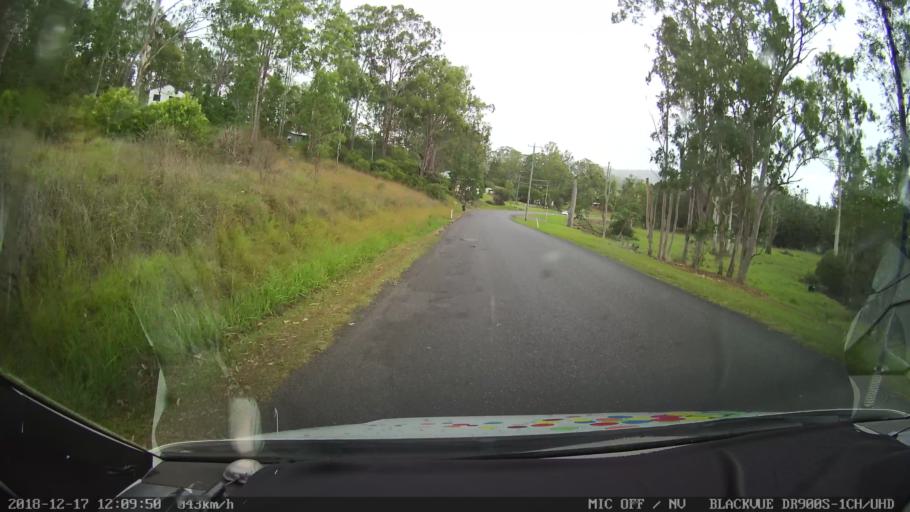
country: AU
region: New South Wales
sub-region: Kyogle
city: Kyogle
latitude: -28.4708
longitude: 152.5481
